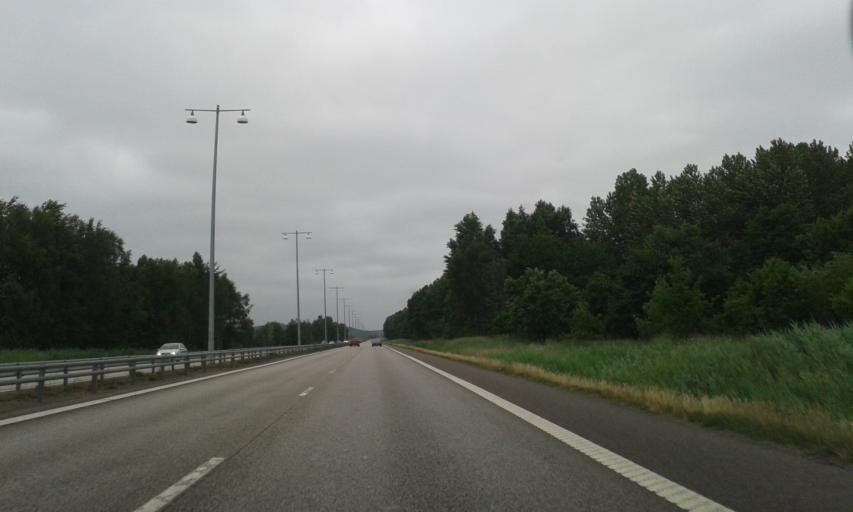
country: SE
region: Vaestra Goetaland
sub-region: Goteborg
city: Hammarkullen
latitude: 57.7715
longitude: 12.0089
